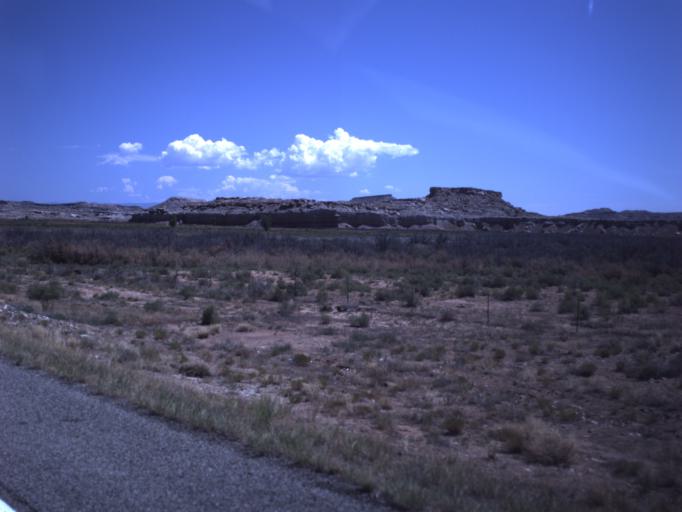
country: US
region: Utah
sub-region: Carbon County
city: East Carbon City
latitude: 38.8470
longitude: -110.3792
